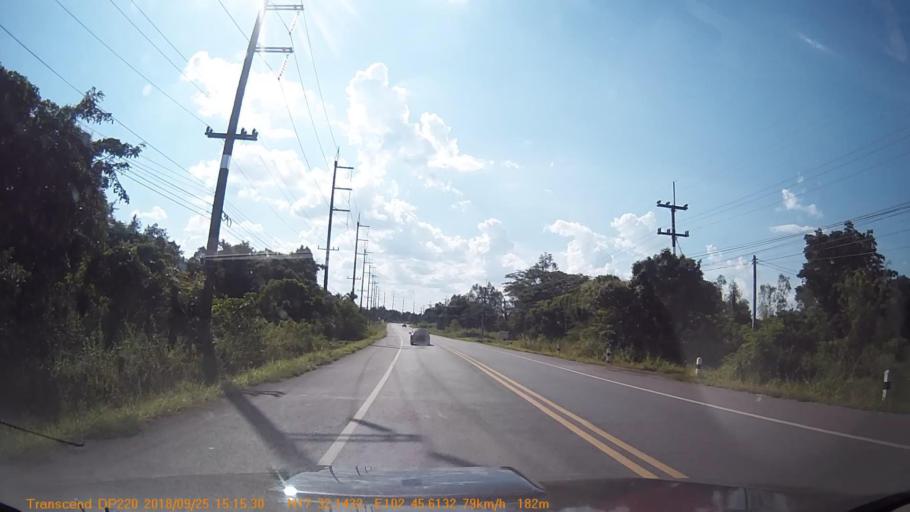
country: TH
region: Changwat Udon Thani
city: Udon Thani
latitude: 17.5358
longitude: 102.7598
